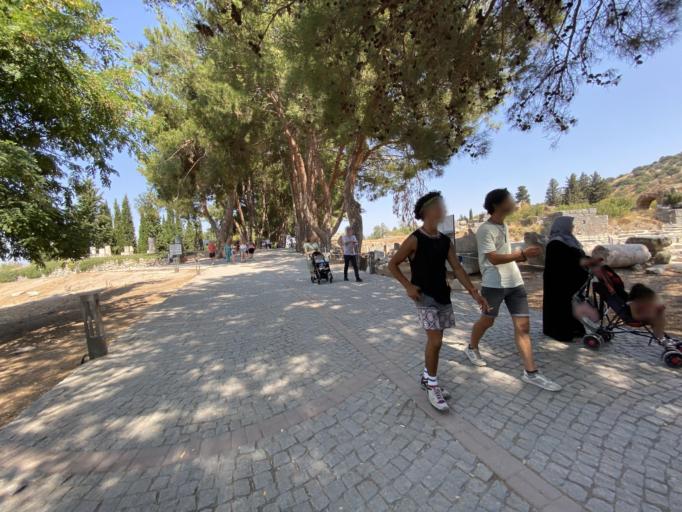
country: TR
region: Izmir
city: Selcuk
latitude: 37.9420
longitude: 27.3411
